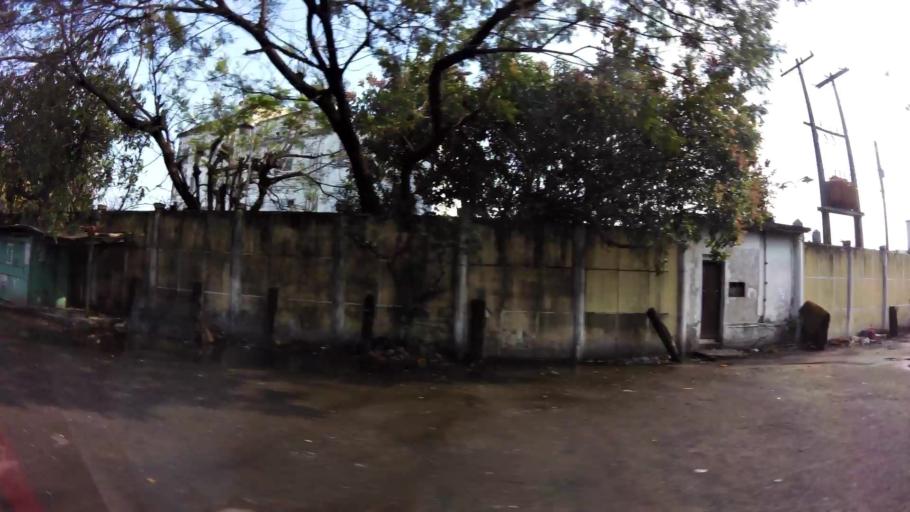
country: PY
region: Asuncion
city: Asuncion
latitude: -25.2765
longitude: -57.6414
